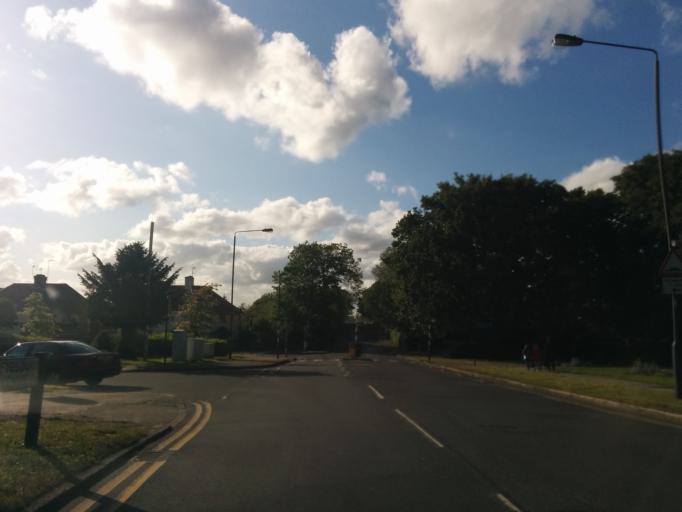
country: GB
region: England
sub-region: Greater London
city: Greenhill
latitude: 51.5754
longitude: -0.3577
